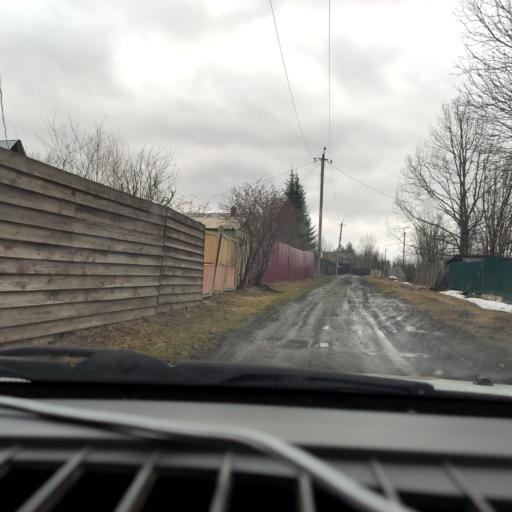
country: RU
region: Perm
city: Novyye Lyady
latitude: 58.1735
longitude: 56.5978
